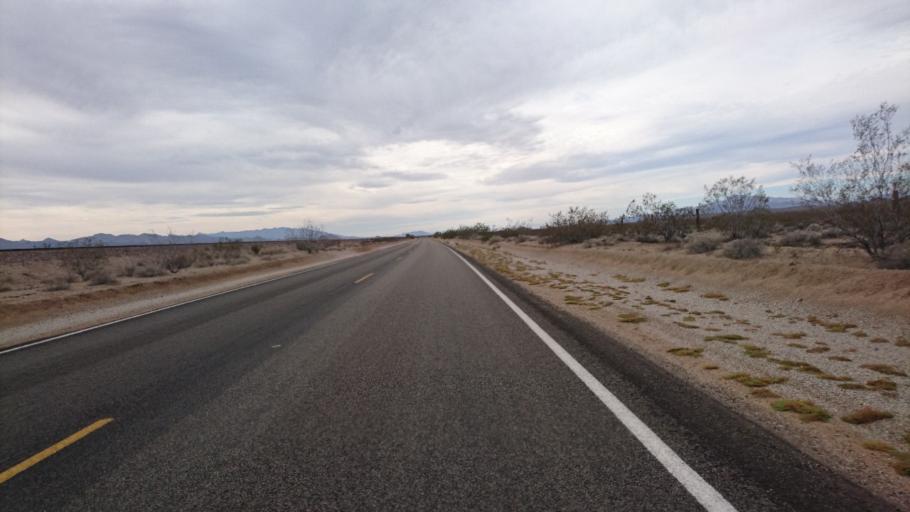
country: US
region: California
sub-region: San Bernardino County
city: Needles
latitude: 34.8730
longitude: -115.1113
